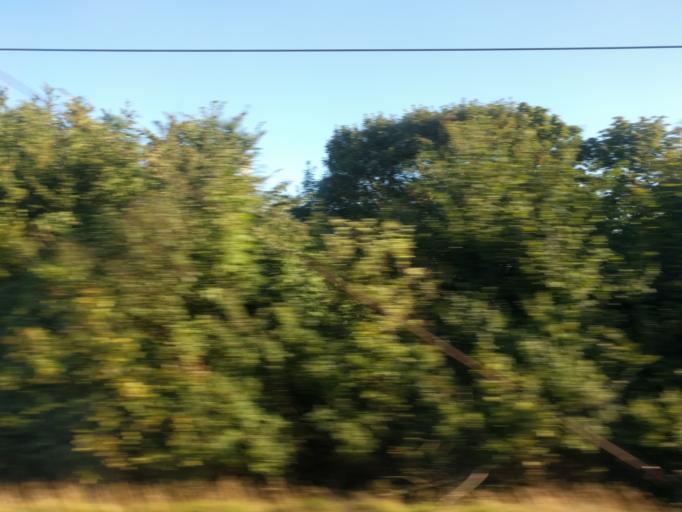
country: DK
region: Zealand
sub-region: Ringsted Kommune
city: Ringsted
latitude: 55.4441
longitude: 11.6817
